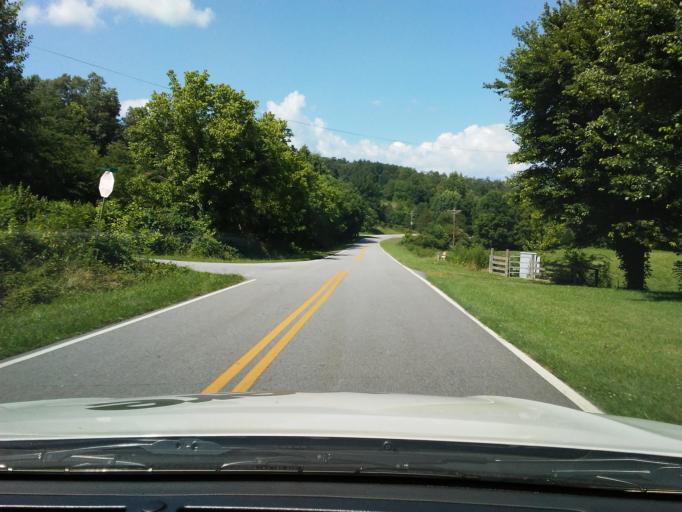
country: US
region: Georgia
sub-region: Towns County
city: Hiawassee
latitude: 34.9390
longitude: -83.8662
